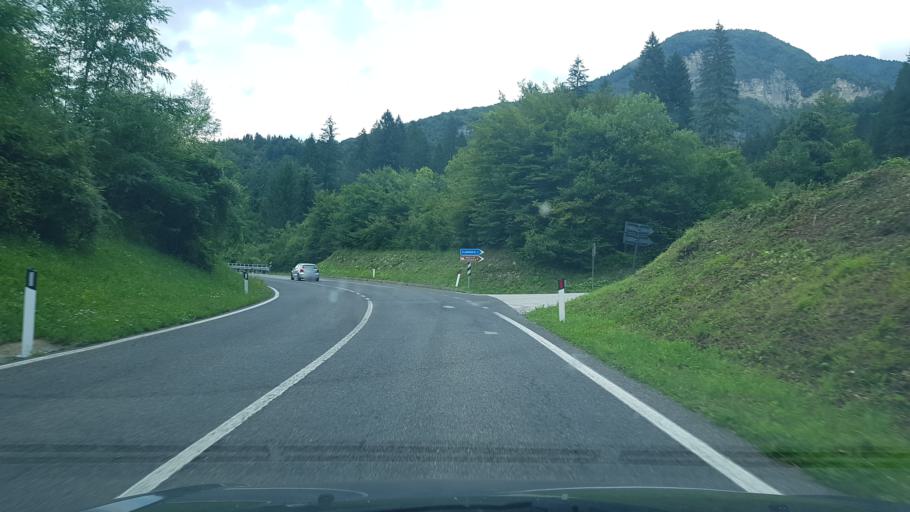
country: IT
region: Friuli Venezia Giulia
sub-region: Provincia di Udine
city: Ovaro
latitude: 46.4650
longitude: 12.8741
